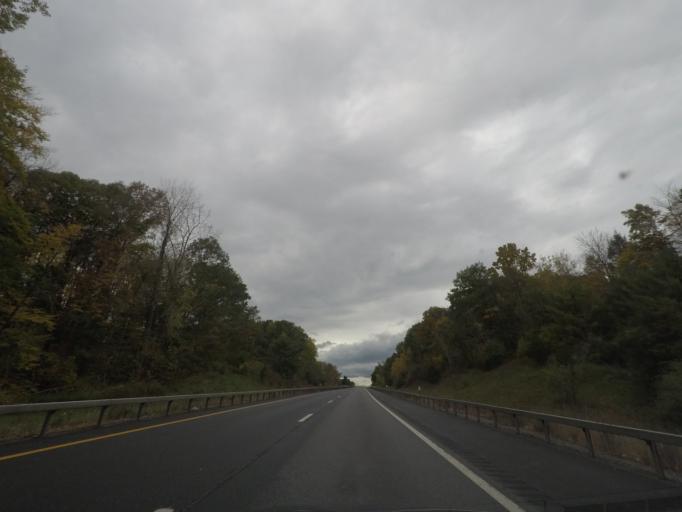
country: US
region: New York
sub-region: Rensselaer County
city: Castleton-on-Hudson
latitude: 42.4980
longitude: -73.7324
